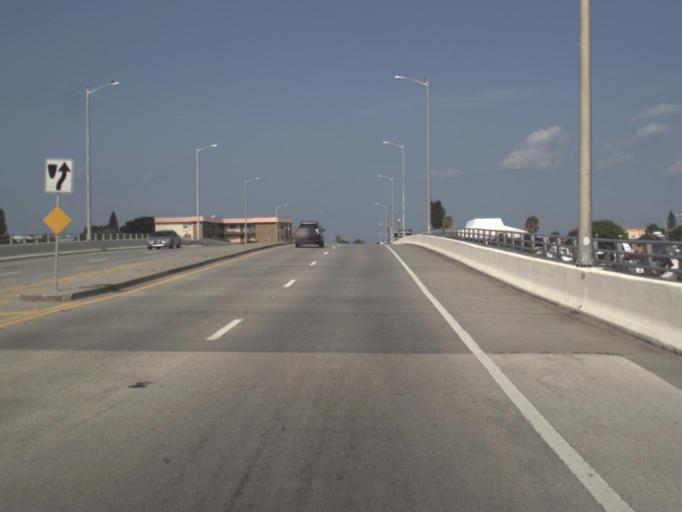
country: US
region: Florida
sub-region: Pinellas County
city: Treasure Island
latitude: 27.7564
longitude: -82.7599
